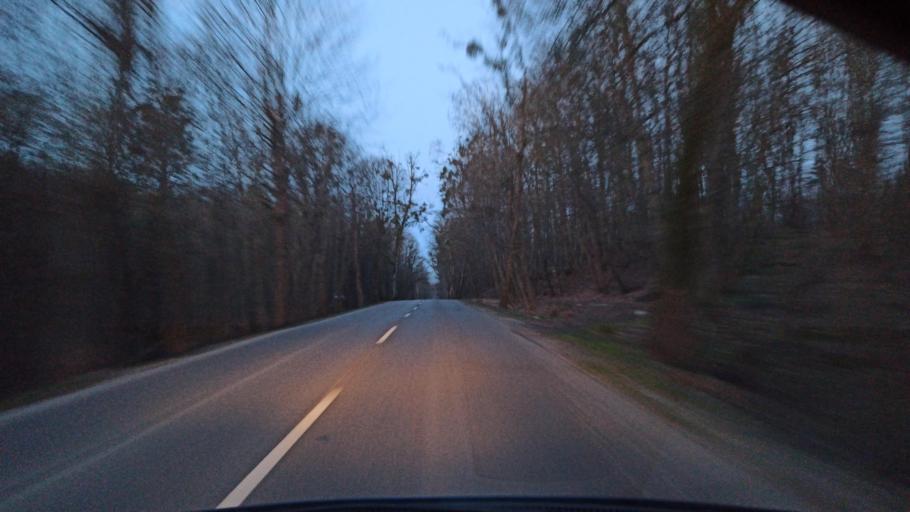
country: PL
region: Warmian-Masurian Voivodeship
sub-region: Powiat elblaski
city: Gronowo Gorne
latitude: 54.1848
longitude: 19.4549
